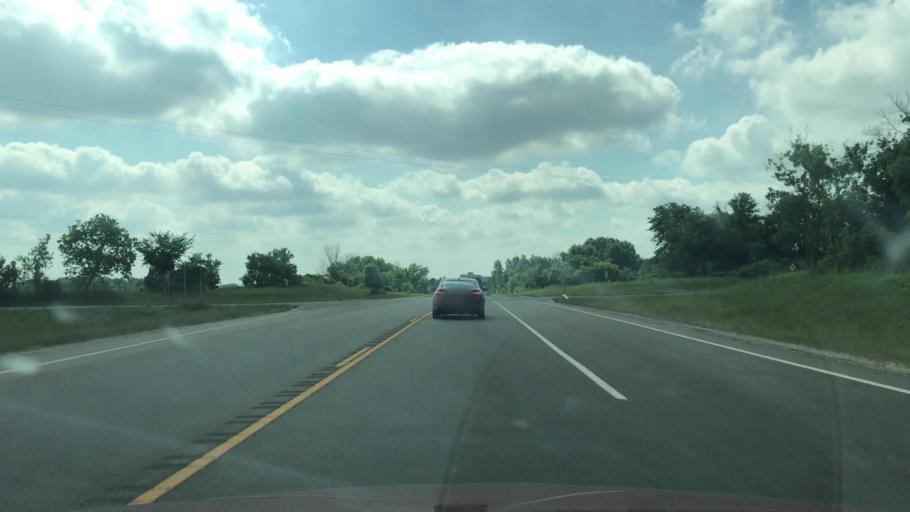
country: US
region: Michigan
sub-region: Kent County
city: Kent City
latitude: 43.2072
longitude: -85.7419
